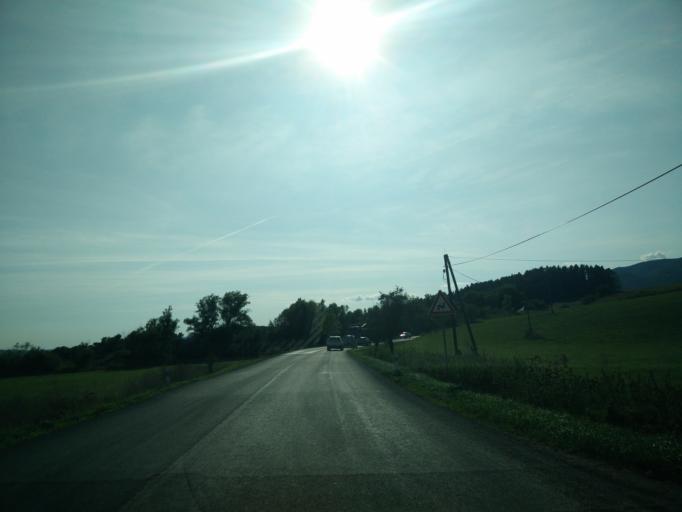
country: SK
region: Zilinsky
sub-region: Okres Martin
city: Martin
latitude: 48.9480
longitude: 18.8417
